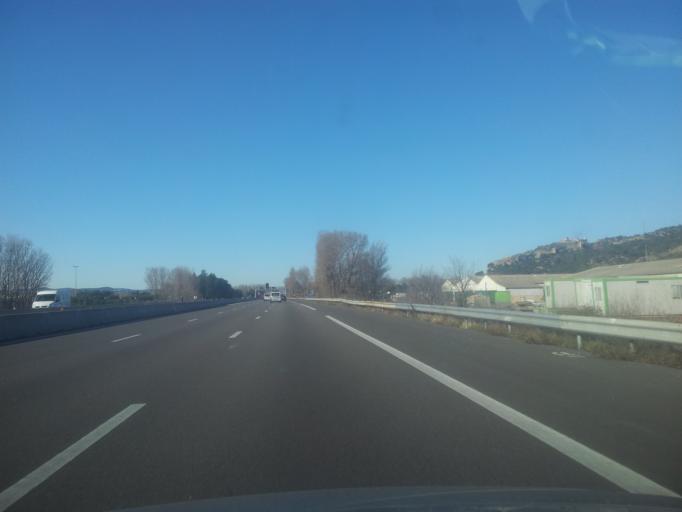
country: FR
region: Provence-Alpes-Cote d'Azur
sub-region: Departement du Vaucluse
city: Mornas
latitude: 44.1941
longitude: 4.7378
